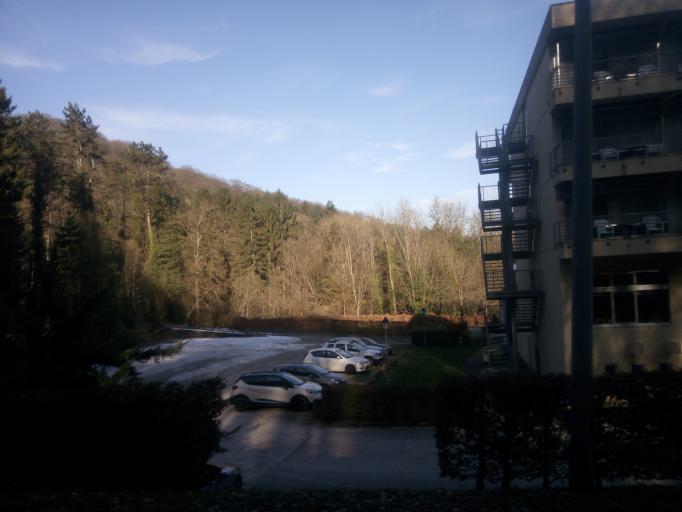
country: LU
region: Grevenmacher
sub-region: Canton d'Echternach
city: Echternach
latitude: 49.8195
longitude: 6.3948
